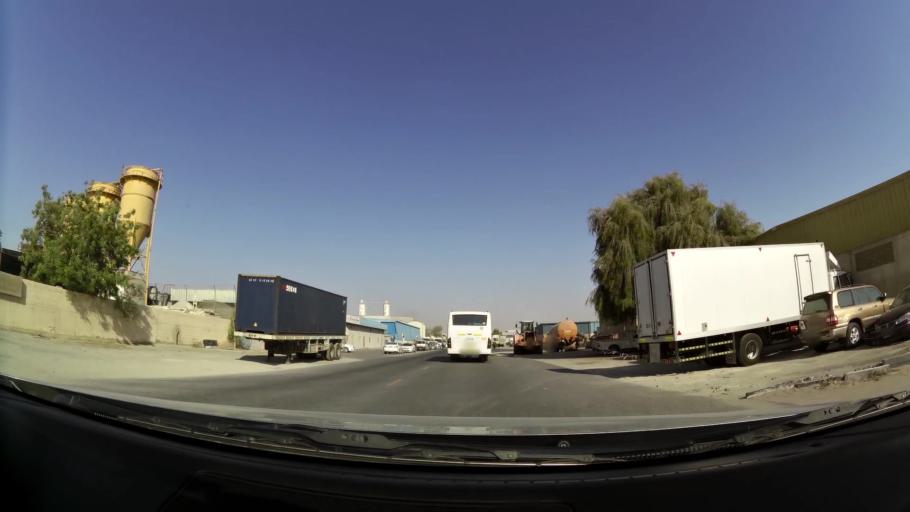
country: AE
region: Dubai
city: Dubai
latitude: 25.1215
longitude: 55.2156
